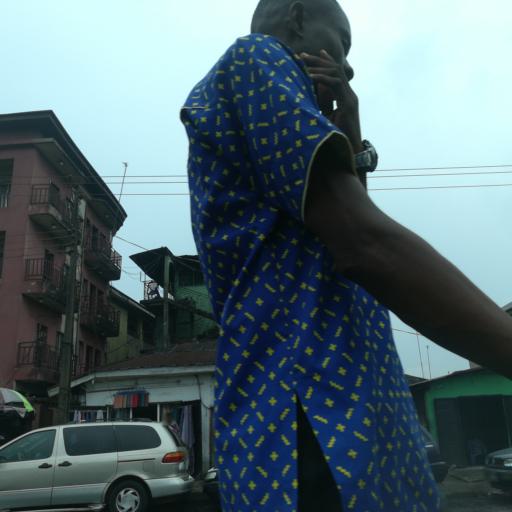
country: NG
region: Rivers
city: Port Harcourt
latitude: 4.7969
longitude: 6.9931
